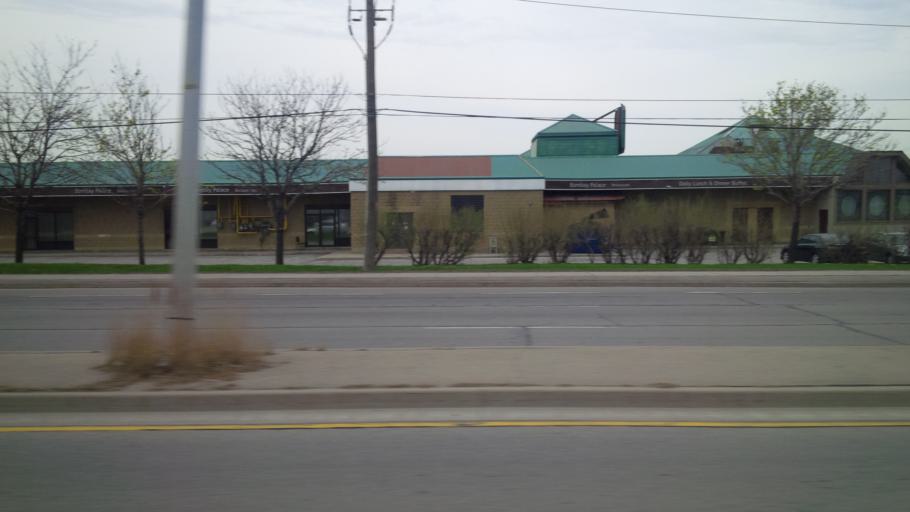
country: CA
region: Ontario
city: Brampton
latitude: 43.6914
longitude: -79.6963
